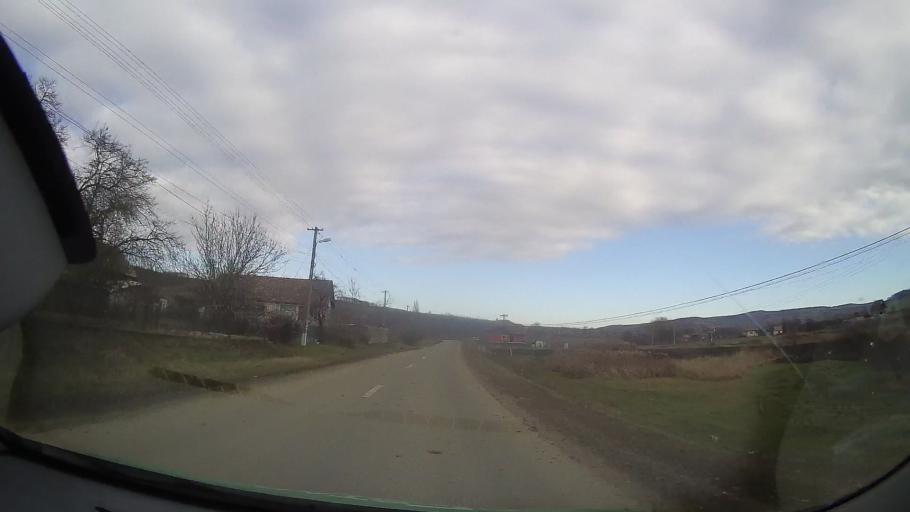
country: RO
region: Mures
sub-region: Comuna Iernut
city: Iernut
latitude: 46.4812
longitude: 24.2297
